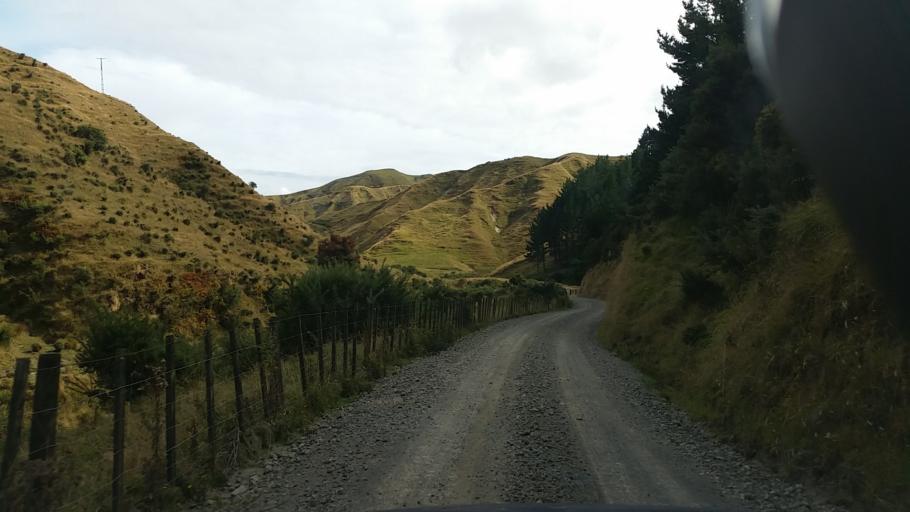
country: NZ
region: Taranaki
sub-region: South Taranaki District
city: Eltham
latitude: -39.2229
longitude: 174.4758
